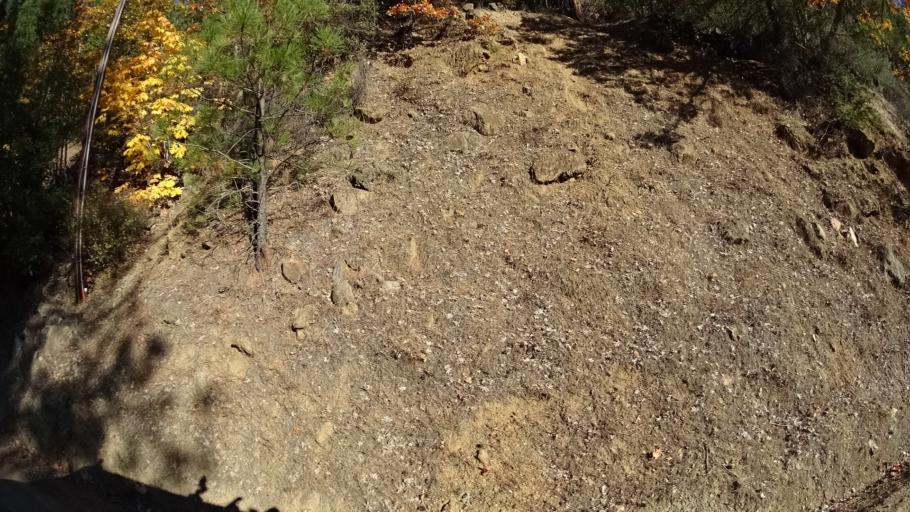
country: US
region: California
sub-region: Siskiyou County
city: Happy Camp
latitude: 41.6355
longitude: -123.0968
